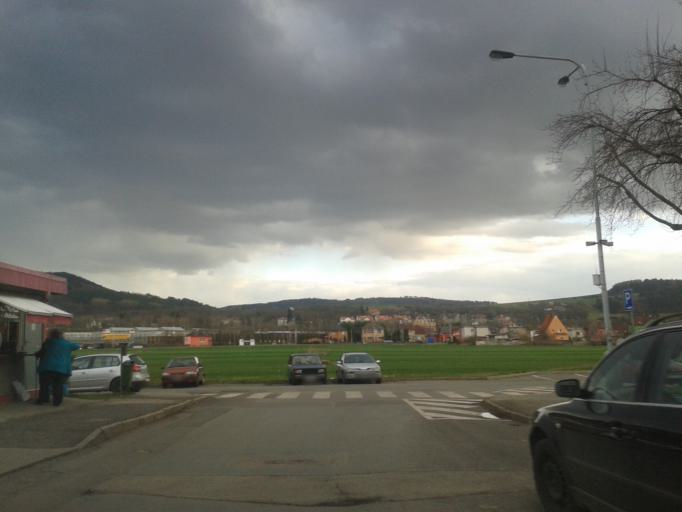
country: CZ
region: Central Bohemia
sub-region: Okres Beroun
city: Kraluv Dvur
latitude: 49.9462
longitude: 14.0279
